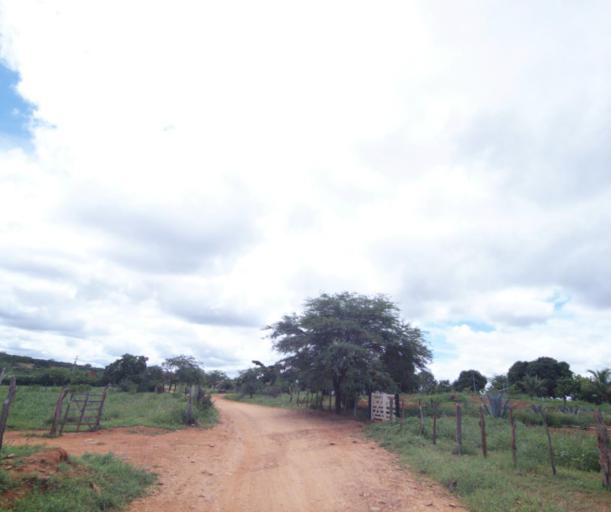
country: BR
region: Bahia
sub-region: Tanhacu
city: Tanhacu
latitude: -14.1569
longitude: -41.1883
